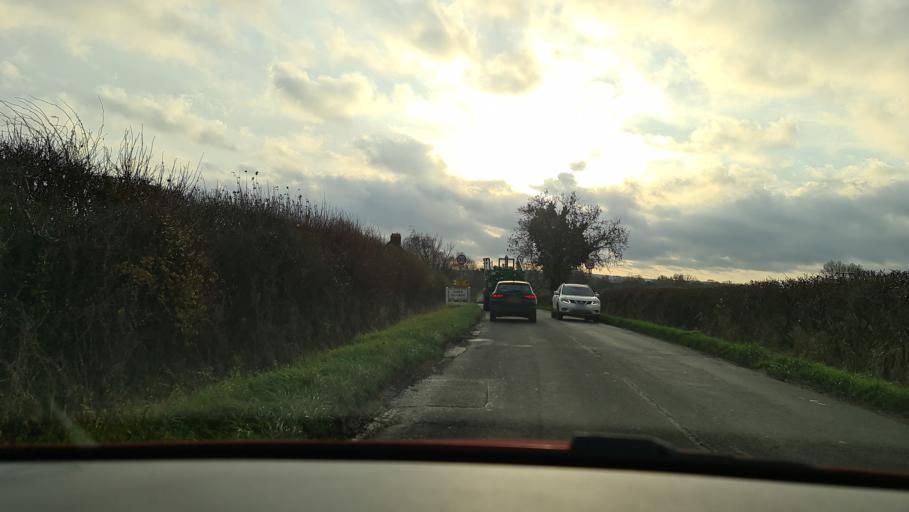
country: GB
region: England
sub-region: Buckinghamshire
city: Stone
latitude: 51.7810
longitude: -0.8787
